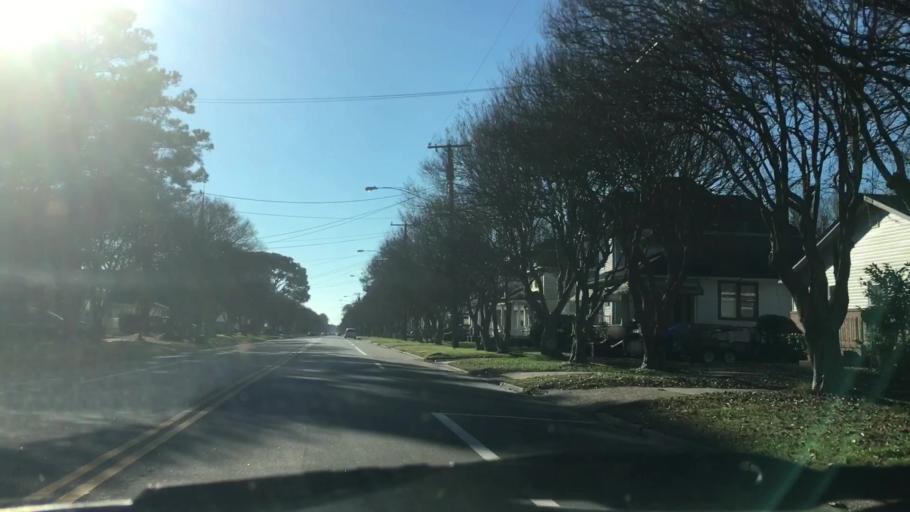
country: US
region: Virginia
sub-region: City of Norfolk
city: Norfolk
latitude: 36.8730
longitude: -76.2530
